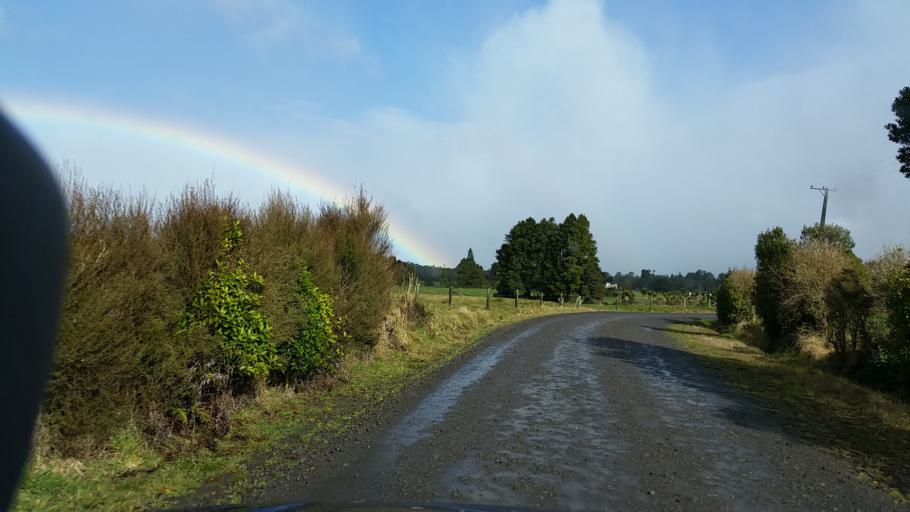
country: NZ
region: Taranaki
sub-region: South Taranaki District
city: Eltham
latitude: -39.2866
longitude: 174.1864
